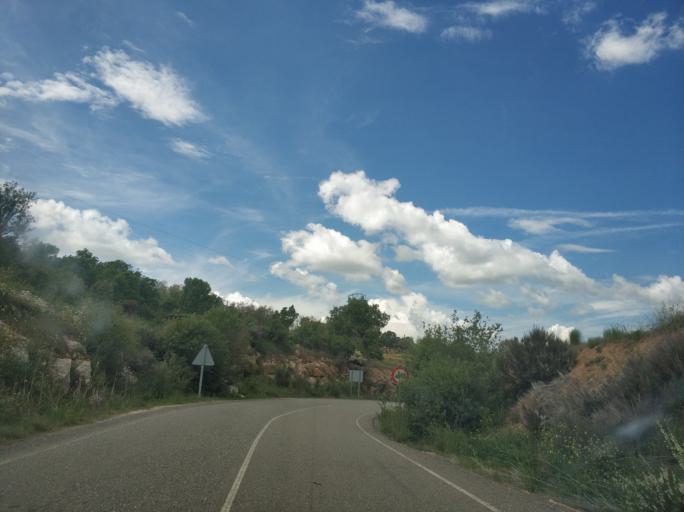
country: ES
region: Castille and Leon
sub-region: Provincia de Salamanca
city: Nava de Bejar
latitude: 40.4628
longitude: -5.6786
